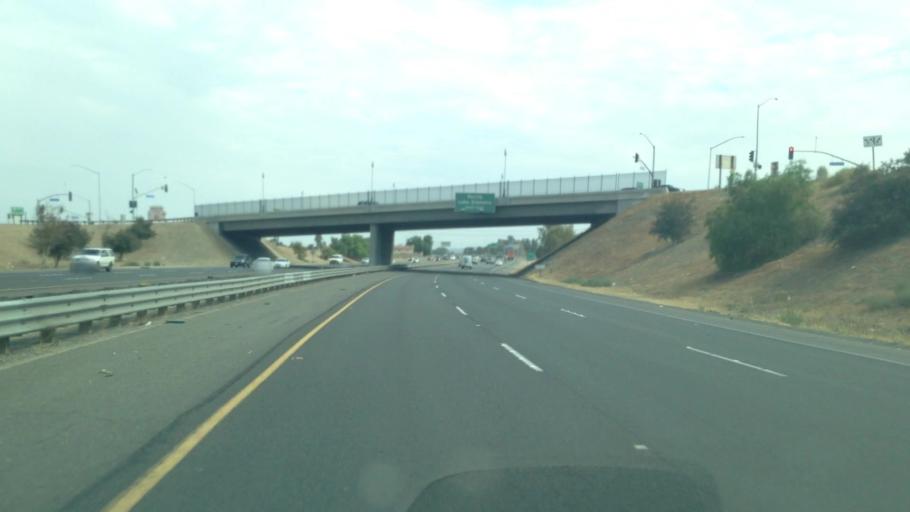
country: US
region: California
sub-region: Riverside County
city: Perris
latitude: 33.8039
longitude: -117.2332
